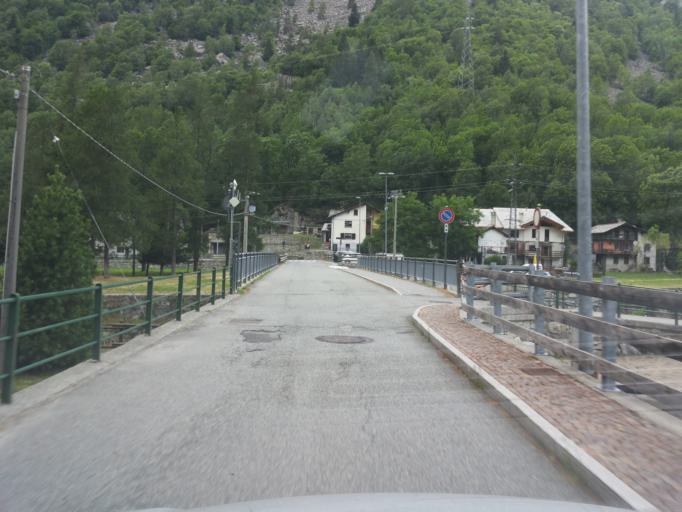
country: IT
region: Aosta Valley
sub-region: Valle d'Aosta
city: Gaby
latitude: 45.7041
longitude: 7.8780
